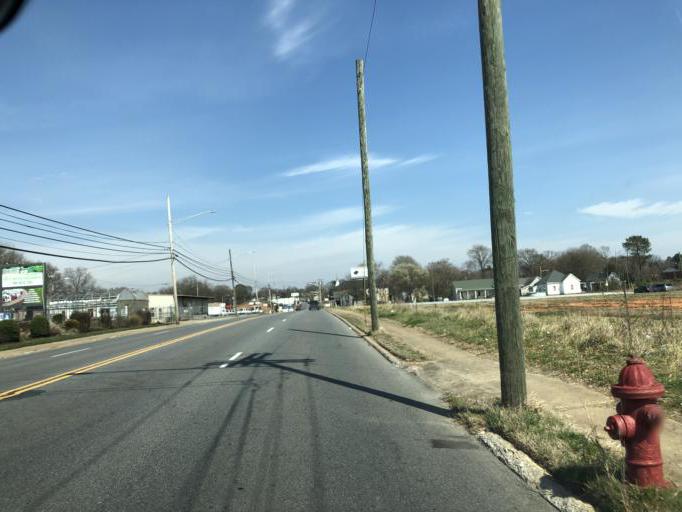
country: US
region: North Carolina
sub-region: Gaston County
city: Ranlo
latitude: 35.2762
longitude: -81.1555
